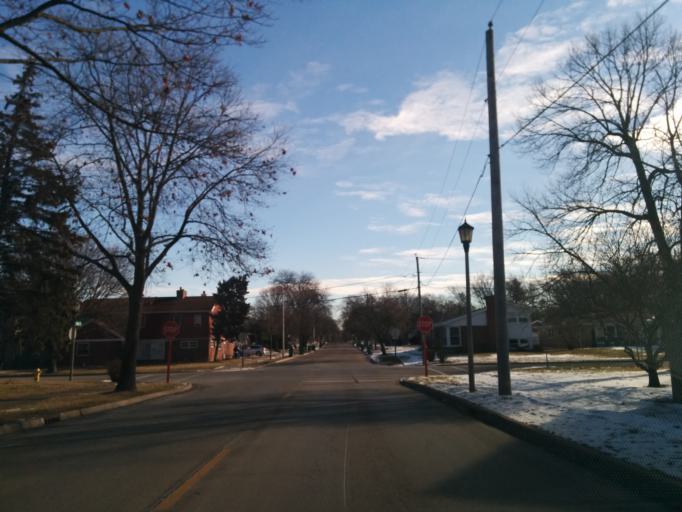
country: US
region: Illinois
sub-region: DuPage County
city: Lombard
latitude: 41.8842
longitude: -88.0089
